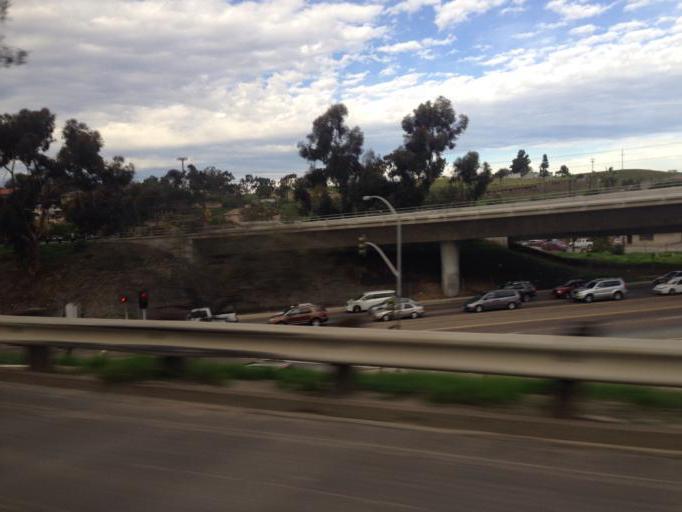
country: US
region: California
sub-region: San Diego County
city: Chula Vista
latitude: 32.6603
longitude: -117.0759
